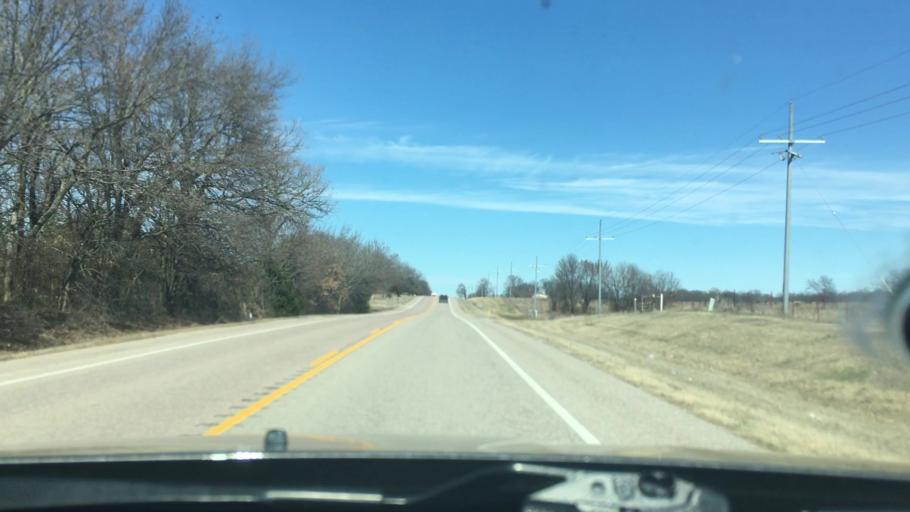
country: US
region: Oklahoma
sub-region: Murray County
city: Sulphur
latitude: 34.4118
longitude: -96.9508
